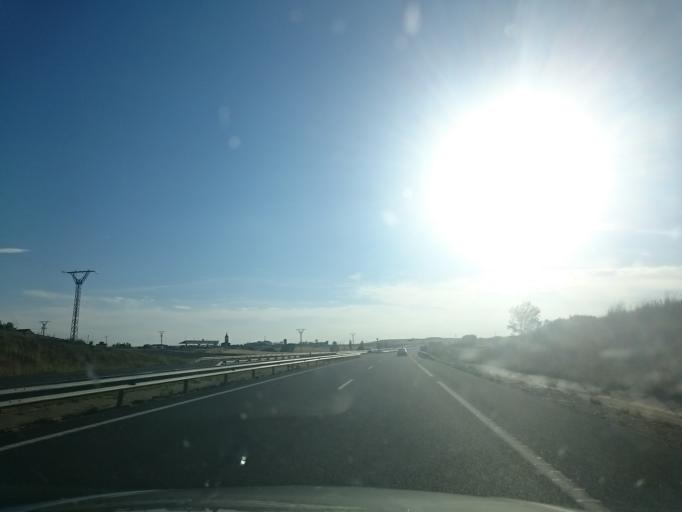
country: ES
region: Castille and Leon
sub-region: Provincia de Palencia
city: Villaherreros
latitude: 42.3926
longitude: -4.4492
